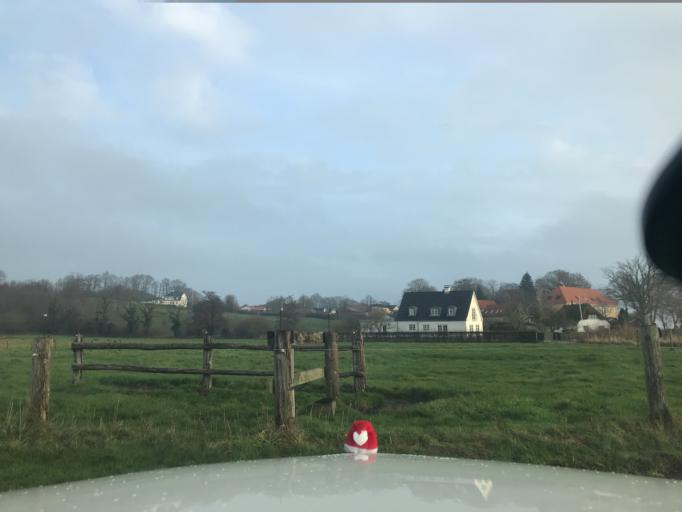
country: DE
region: Schleswig-Holstein
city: Glucksburg
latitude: 54.8714
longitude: 9.5133
